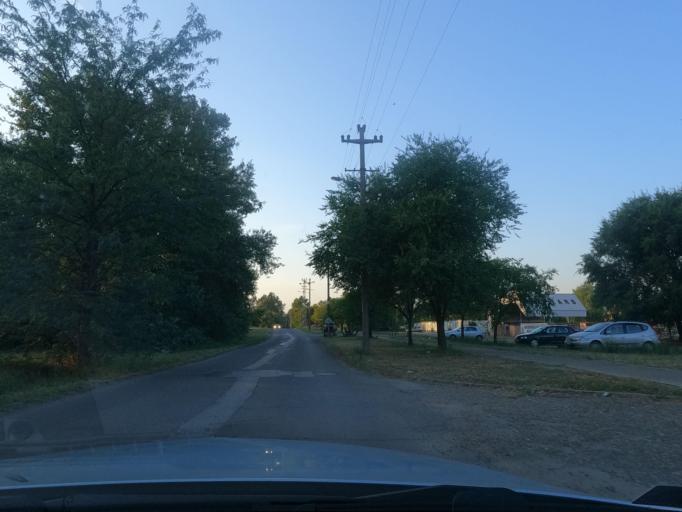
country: RS
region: Autonomna Pokrajina Vojvodina
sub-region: Juznobacki Okrug
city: Novi Sad
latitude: 45.2314
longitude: 19.8277
